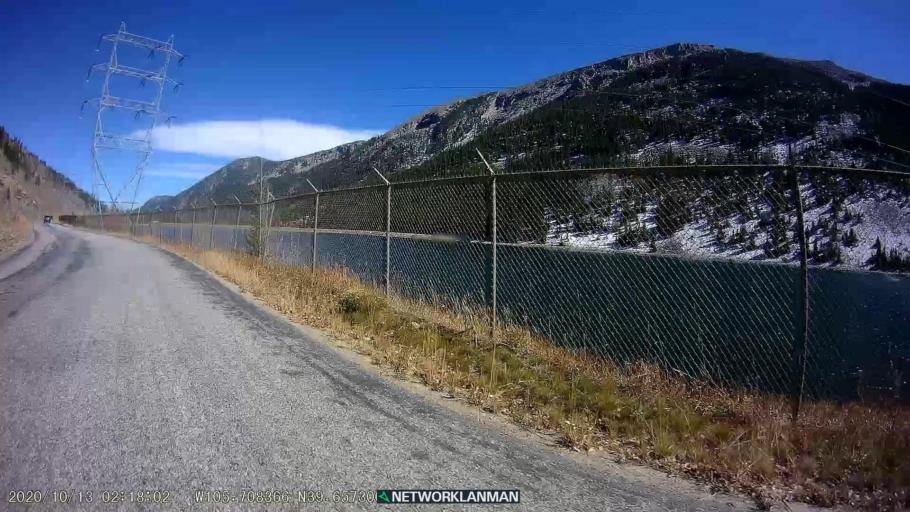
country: US
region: Colorado
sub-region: Clear Creek County
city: Georgetown
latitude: 39.6576
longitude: -105.7084
